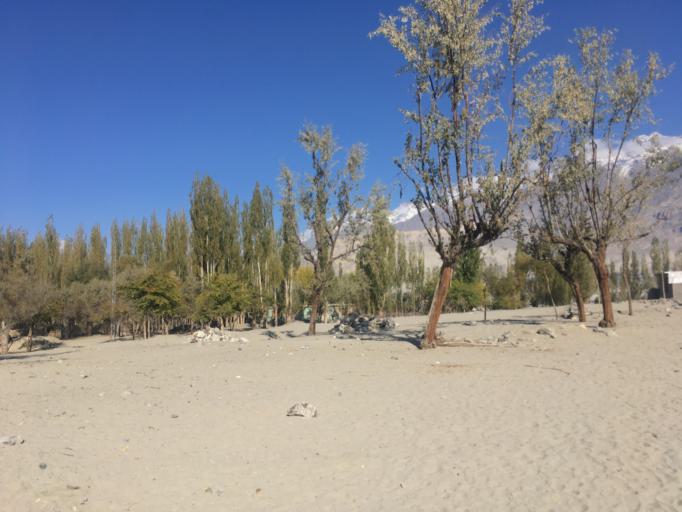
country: PK
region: Gilgit-Baltistan
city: Skardu
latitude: 35.3210
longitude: 75.6051
